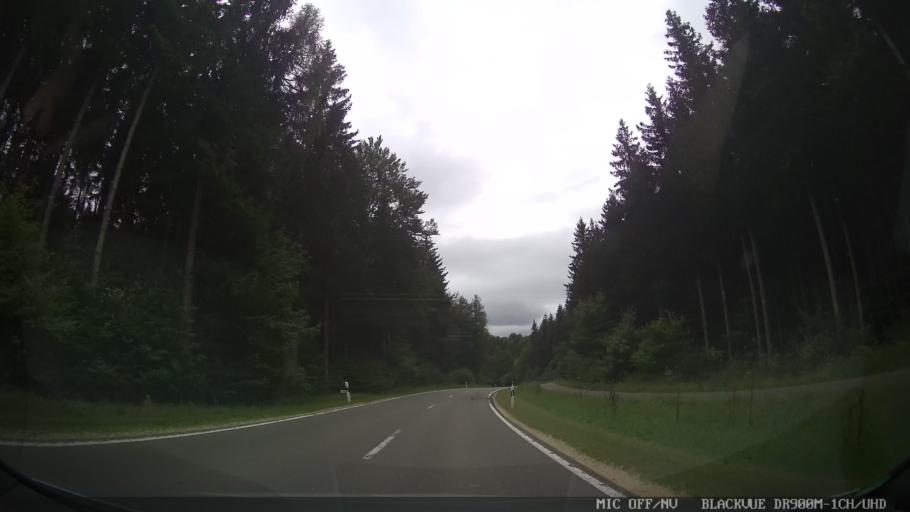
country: DE
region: Baden-Wuerttemberg
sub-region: Freiburg Region
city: Neuhausen ob Eck
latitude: 47.9557
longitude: 8.9360
